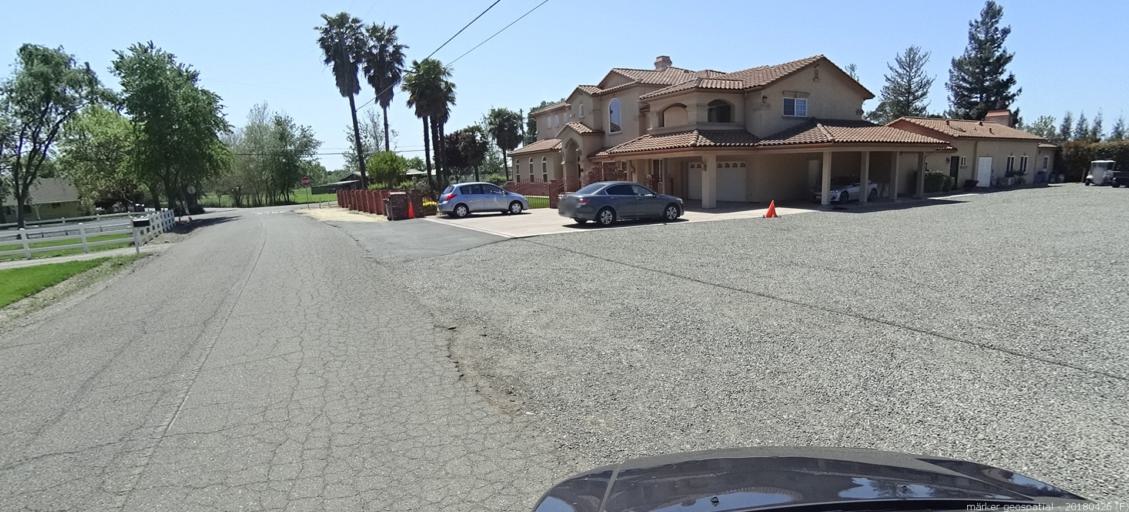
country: US
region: California
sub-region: Yolo County
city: West Sacramento
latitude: 38.5327
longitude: -121.5500
